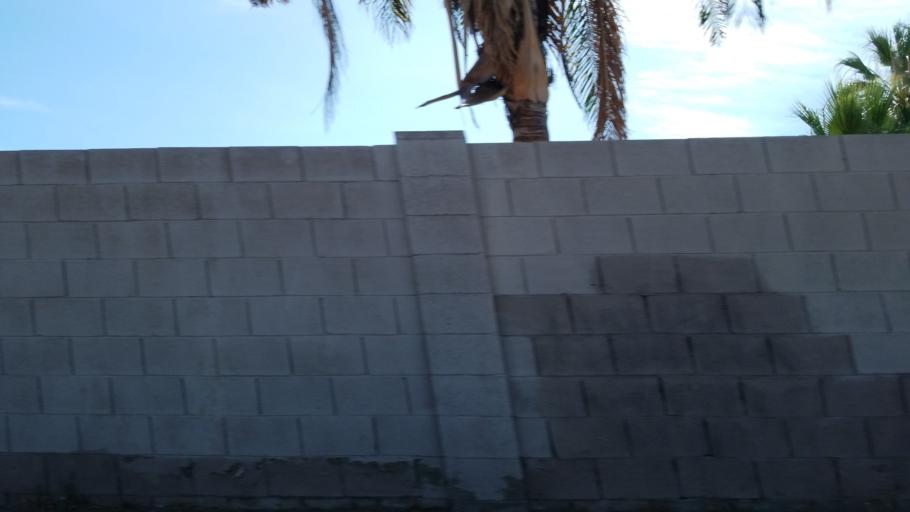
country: US
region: Arizona
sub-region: Maricopa County
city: Glendale
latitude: 33.5873
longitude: -112.1514
